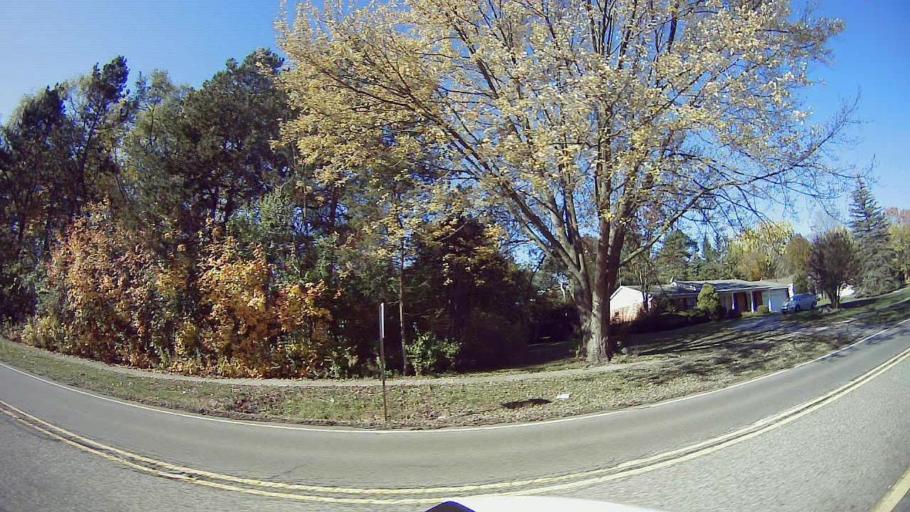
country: US
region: Michigan
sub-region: Oakland County
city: Farmington Hills
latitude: 42.5066
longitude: -83.3785
